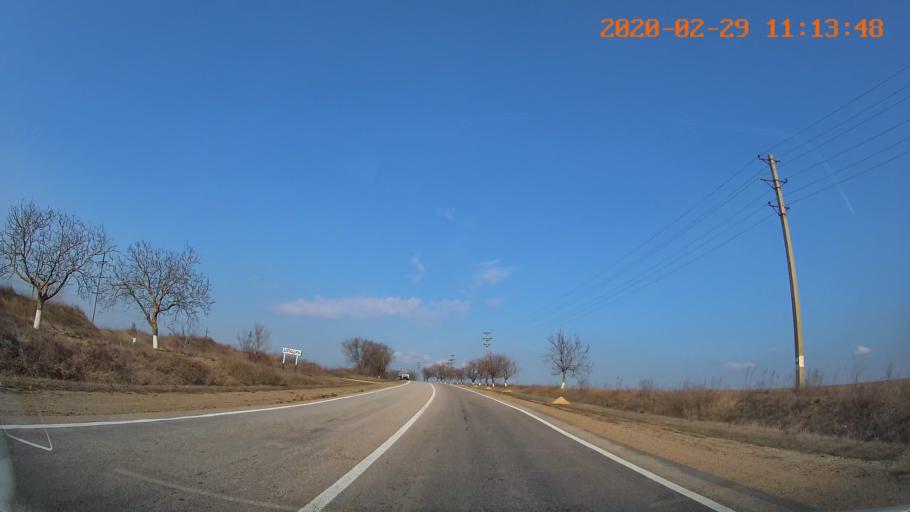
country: MD
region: Telenesti
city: Dubasari
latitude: 47.2758
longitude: 29.1794
